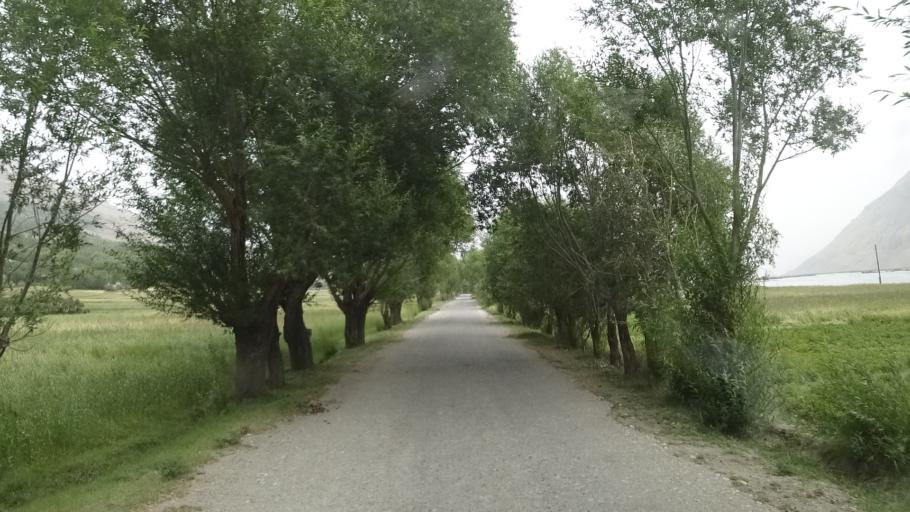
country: AF
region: Badakhshan
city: Khandud
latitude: 37.0304
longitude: 72.6214
